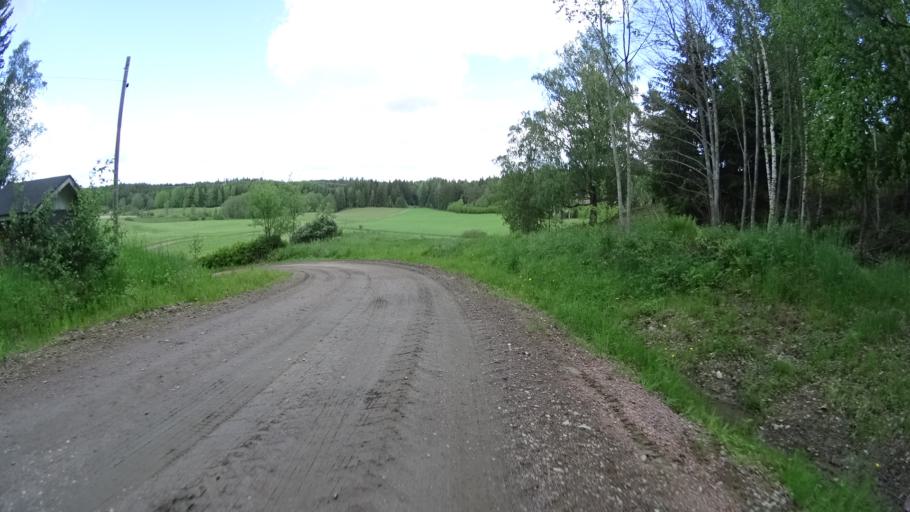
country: FI
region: Uusimaa
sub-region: Raaseporin
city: Karis
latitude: 60.1453
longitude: 23.6203
